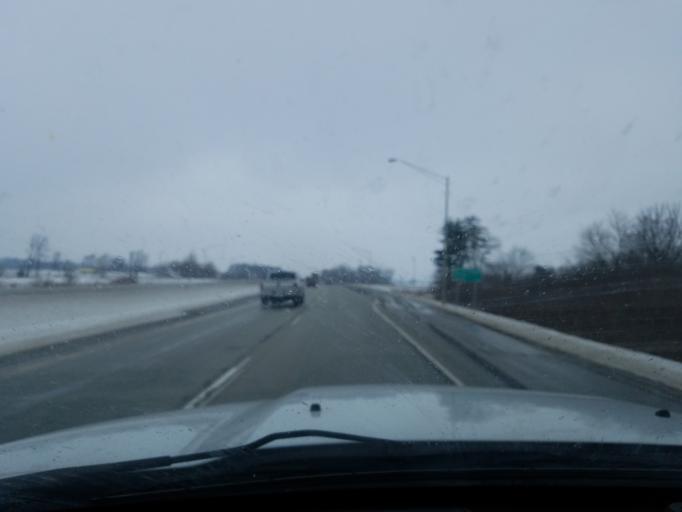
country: US
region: Indiana
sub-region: Marshall County
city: Argos
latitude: 41.1706
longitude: -86.2408
